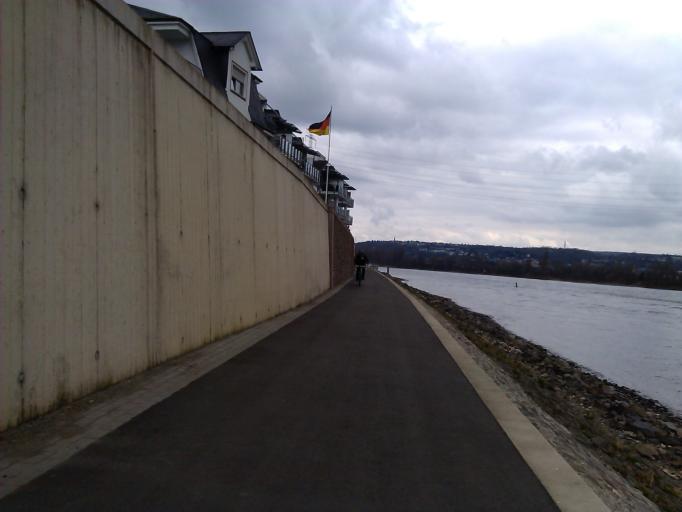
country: DE
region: Rheinland-Pfalz
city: Vallendar
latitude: 50.3805
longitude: 7.6115
